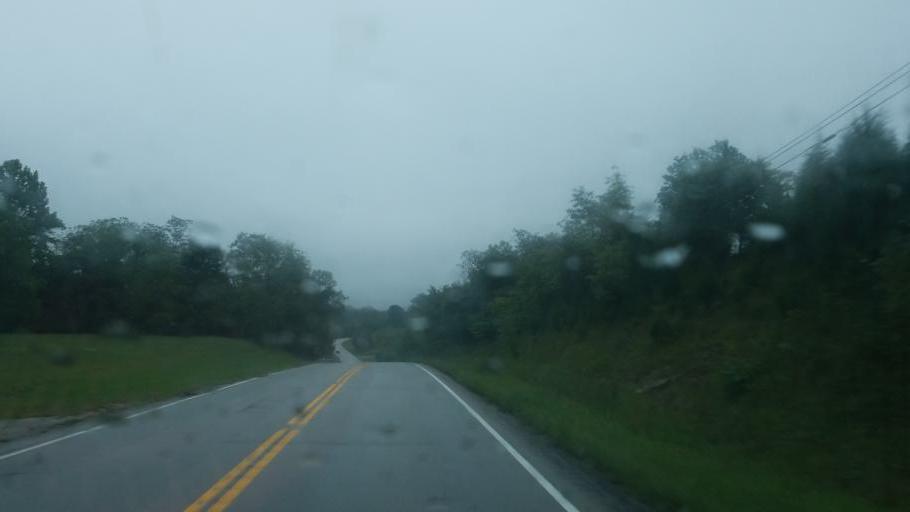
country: US
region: Kentucky
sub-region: Fleming County
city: Flemingsburg
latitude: 38.3794
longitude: -83.6427
